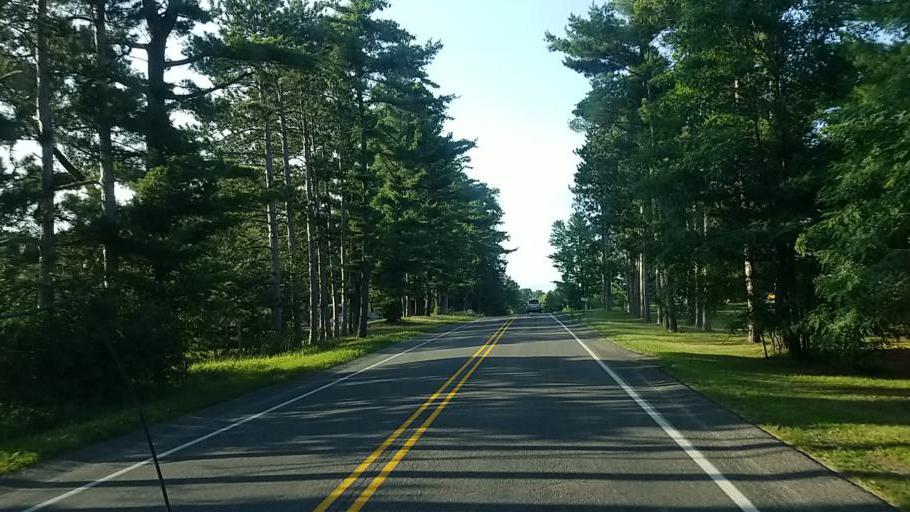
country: US
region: Michigan
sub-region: Montcalm County
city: Greenville
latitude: 43.1826
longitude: -85.3524
